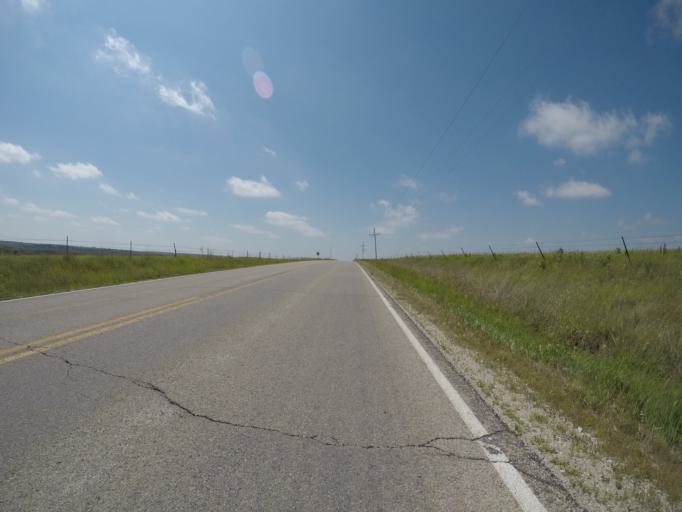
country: US
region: Kansas
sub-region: Pottawatomie County
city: Westmoreland
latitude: 39.3793
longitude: -96.4267
